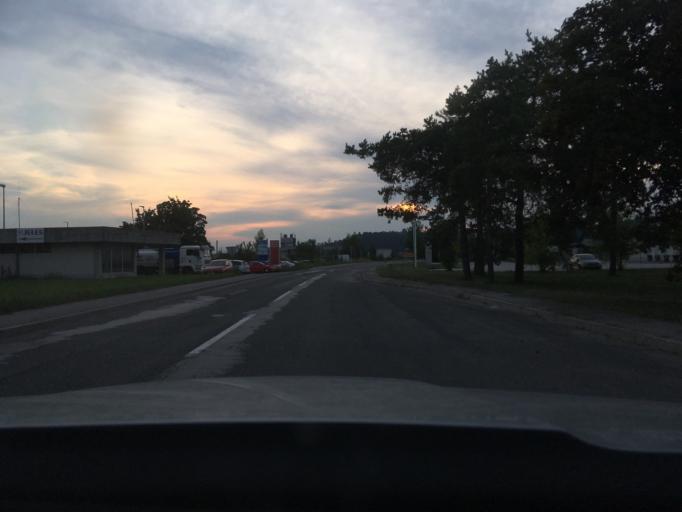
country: SI
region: Kamnik
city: Smarca
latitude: 46.1993
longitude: 14.5871
